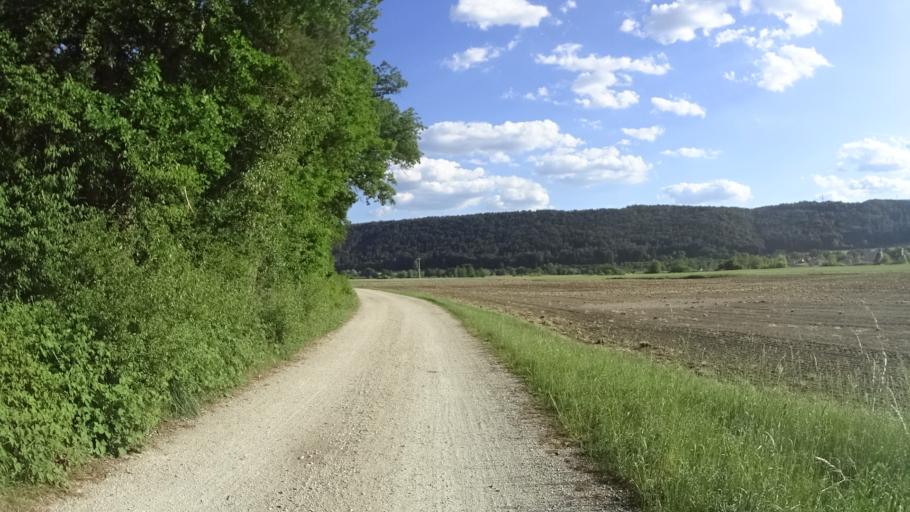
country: DE
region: Bavaria
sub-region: Upper Palatinate
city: Dietfurt
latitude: 49.0262
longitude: 11.5982
